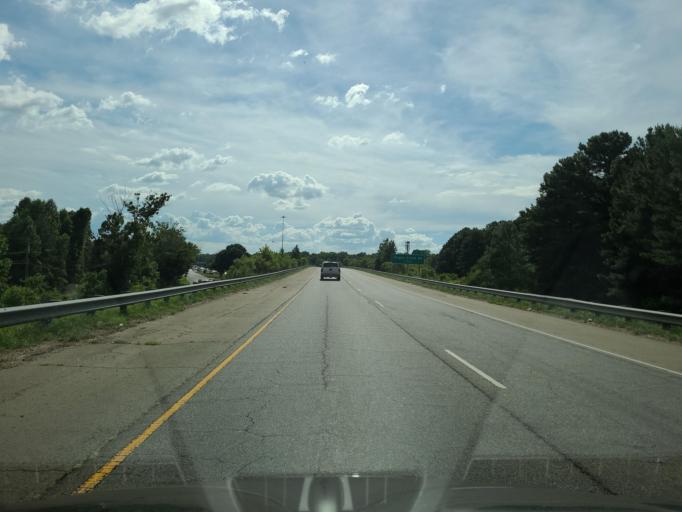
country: US
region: North Carolina
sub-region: Mecklenburg County
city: Charlotte
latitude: 35.2844
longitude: -80.7720
